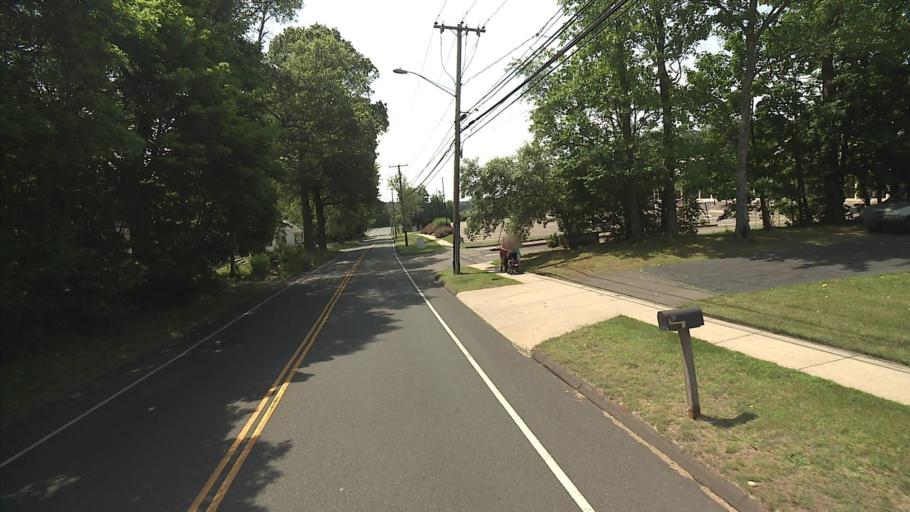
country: US
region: Connecticut
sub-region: New Haven County
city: Branford
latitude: 41.2946
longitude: -72.8198
